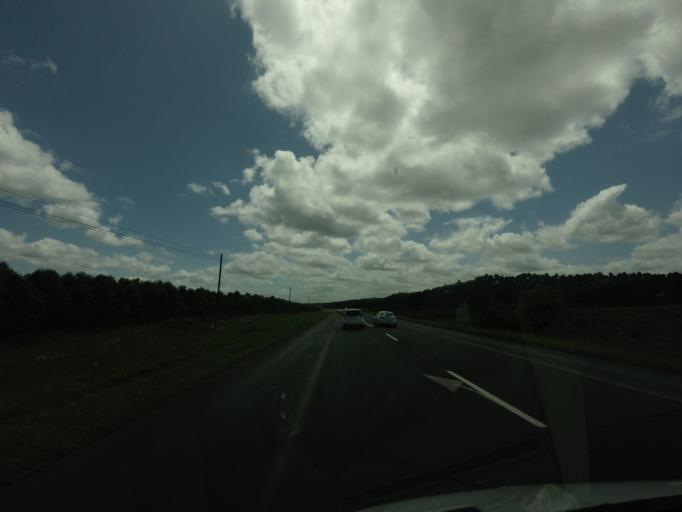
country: ZA
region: KwaZulu-Natal
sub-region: uThungulu District Municipality
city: KwaMbonambi
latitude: -28.5702
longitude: 32.1106
